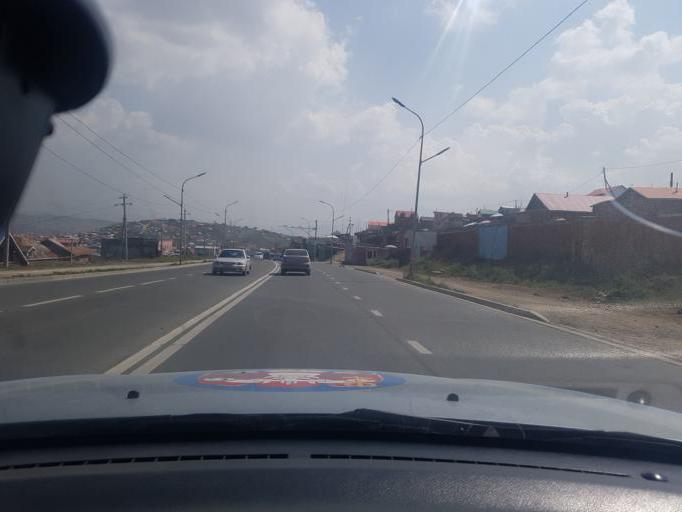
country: MN
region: Ulaanbaatar
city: Ulaanbaatar
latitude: 47.9446
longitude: 106.8721
